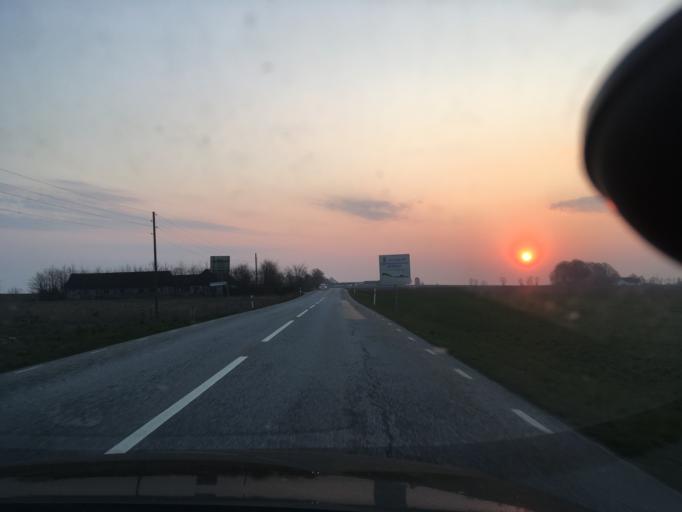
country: SE
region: Skane
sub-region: Tomelilla Kommun
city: Tomelilla
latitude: 55.4796
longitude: 14.0748
